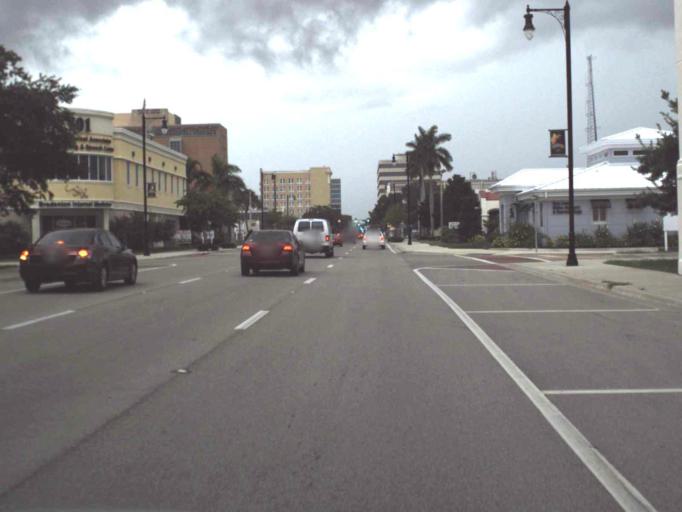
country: US
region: Florida
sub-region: Manatee County
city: Bradenton
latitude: 27.4954
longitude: -82.5681
